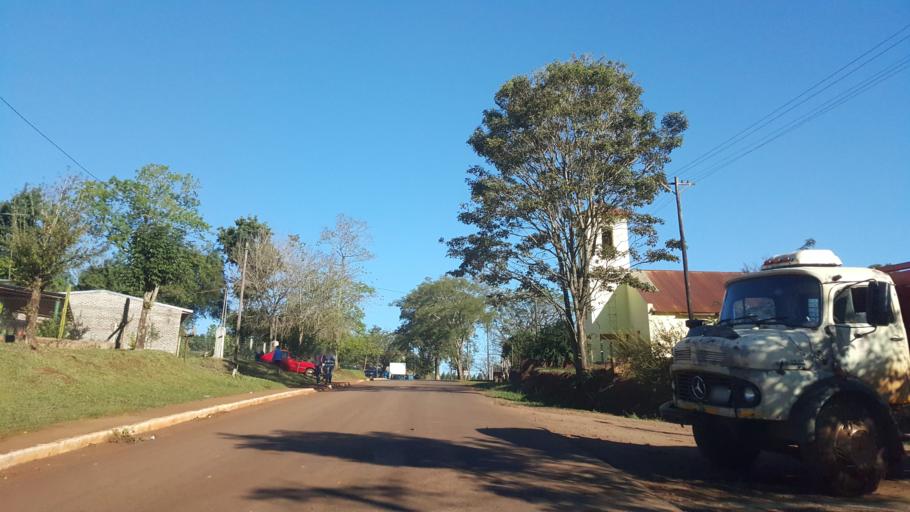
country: AR
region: Misiones
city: Jardin America
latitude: -27.0908
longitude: -55.2864
